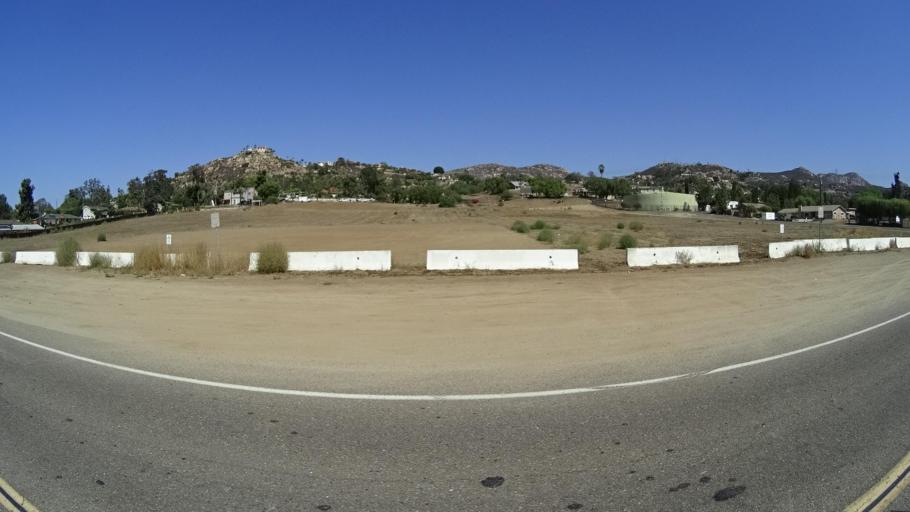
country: US
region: California
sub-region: San Diego County
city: Granite Hills
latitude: 32.8032
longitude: -116.9066
